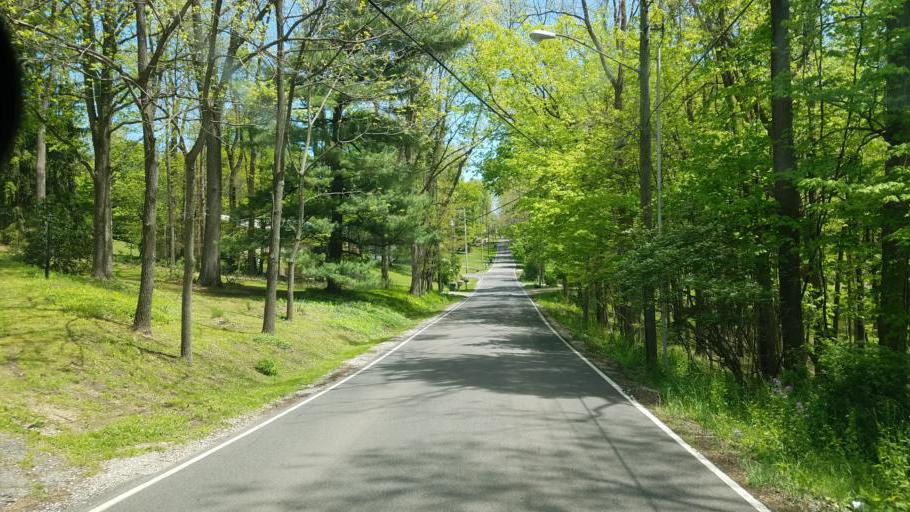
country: US
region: Ohio
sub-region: Knox County
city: Mount Vernon
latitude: 40.3918
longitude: -82.4598
